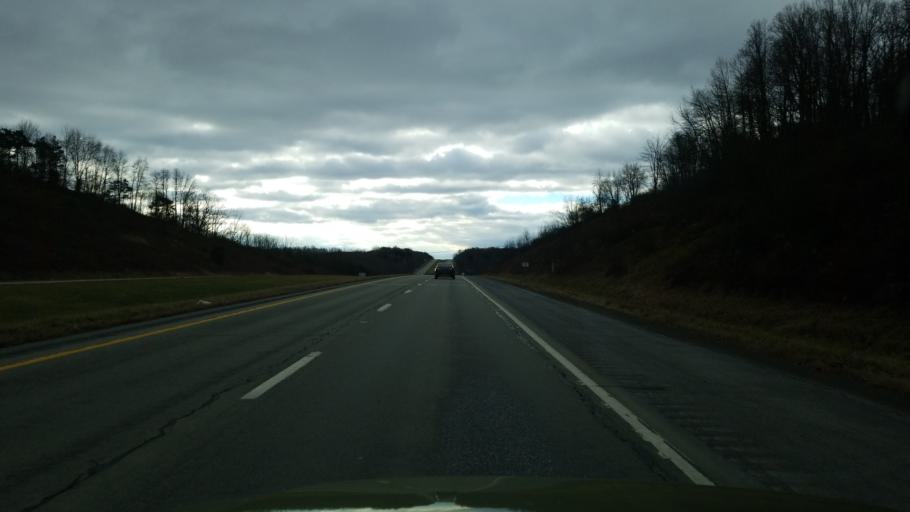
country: US
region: Pennsylvania
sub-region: Indiana County
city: Chevy Chase Heights
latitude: 40.6629
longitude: -79.1144
